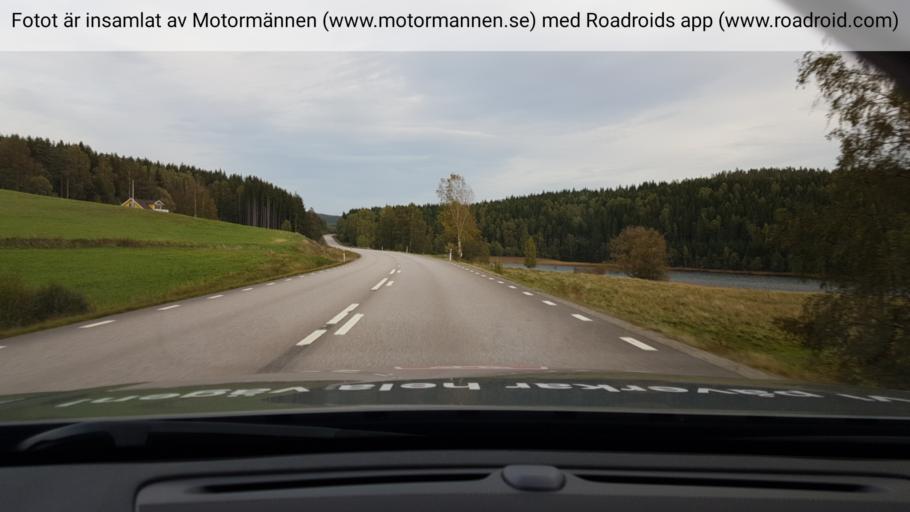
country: SE
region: Vaestra Goetaland
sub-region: Bengtsfors Kommun
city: Billingsfors
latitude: 59.0294
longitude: 12.3402
